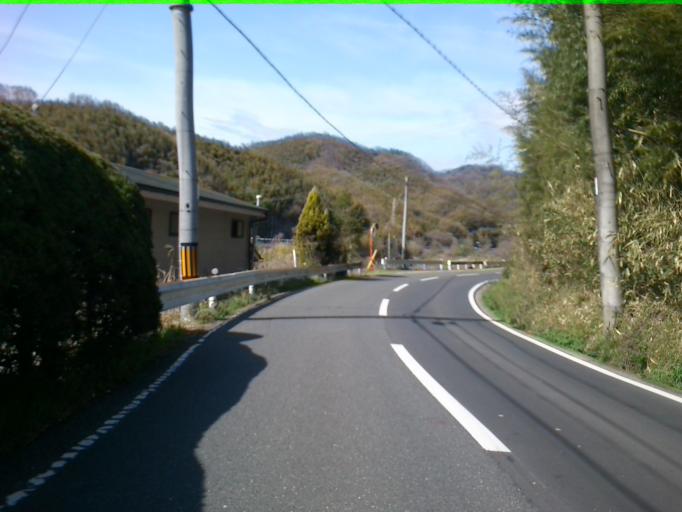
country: JP
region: Nara
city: Nara-shi
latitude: 34.7496
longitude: 135.8364
